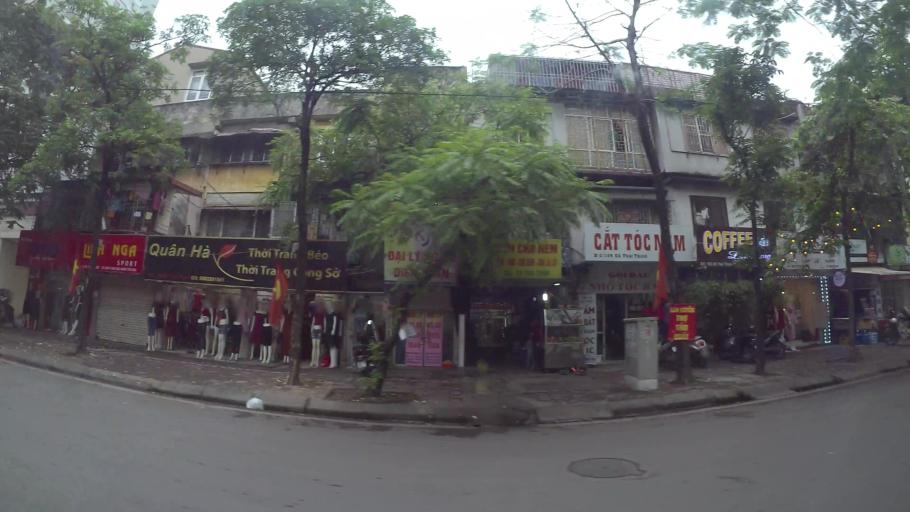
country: VN
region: Ha Noi
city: Dong Da
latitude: 21.0080
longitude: 105.8208
